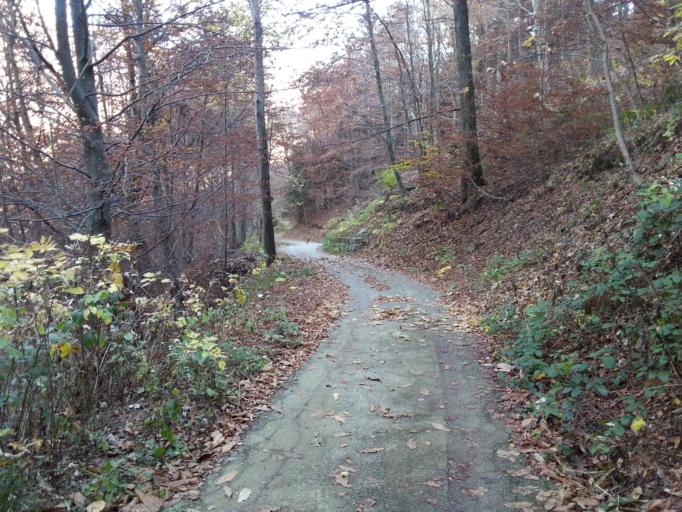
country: IT
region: Lombardy
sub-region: Provincia di Lecco
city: Primaluna
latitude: 45.9765
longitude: 9.4193
